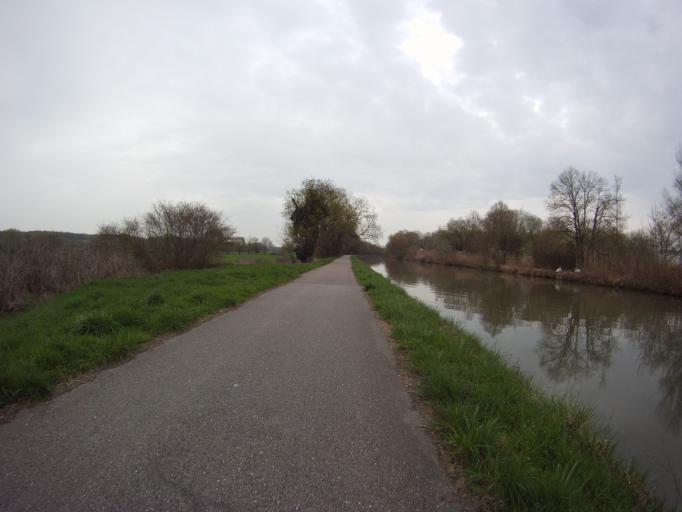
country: FR
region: Lorraine
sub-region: Departement de Meurthe-et-Moselle
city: Jarville-la-Malgrange
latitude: 48.6656
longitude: 6.2193
